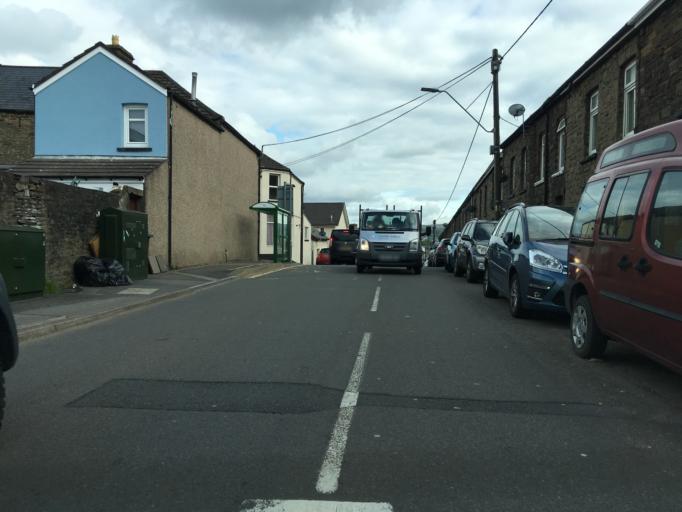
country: GB
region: Wales
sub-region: Merthyr Tydfil County Borough
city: Treharris
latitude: 51.6673
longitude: -3.2963
